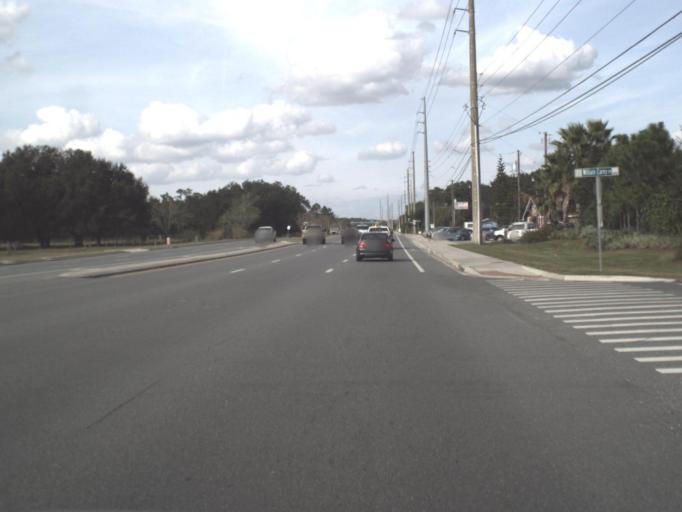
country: US
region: Florida
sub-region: Osceola County
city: Buenaventura Lakes
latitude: 28.3887
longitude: -81.2443
